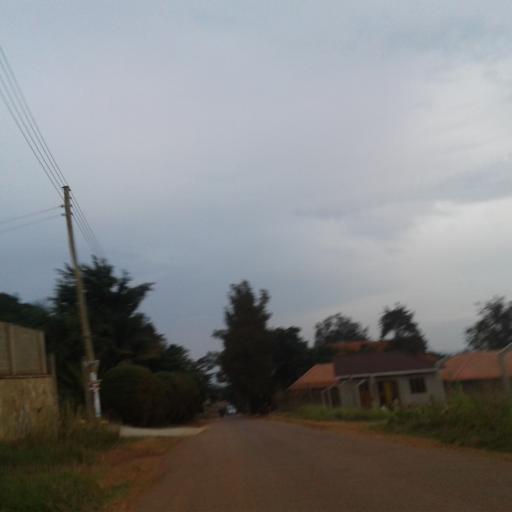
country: UG
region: Central Region
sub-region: Kampala District
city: Kampala
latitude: 0.2487
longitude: 32.6194
